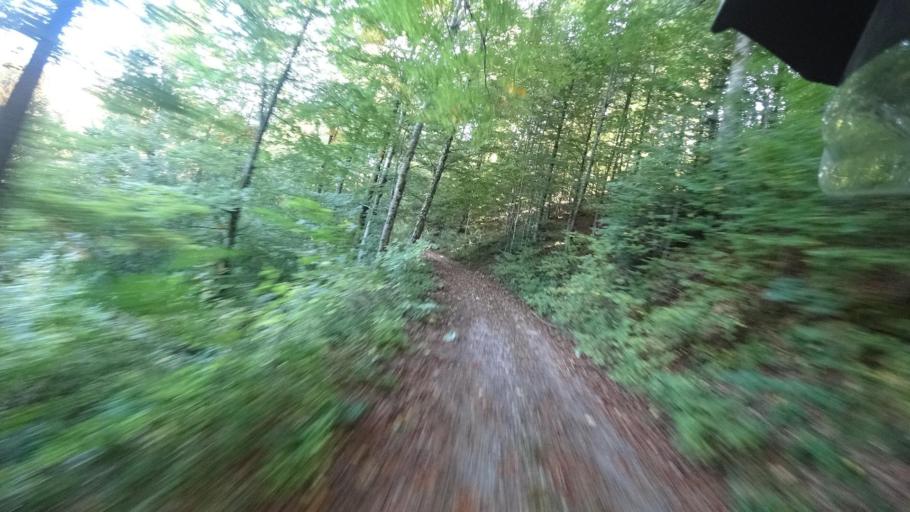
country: HR
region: Karlovacka
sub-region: Grad Ogulin
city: Ogulin
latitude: 45.1770
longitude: 15.1392
